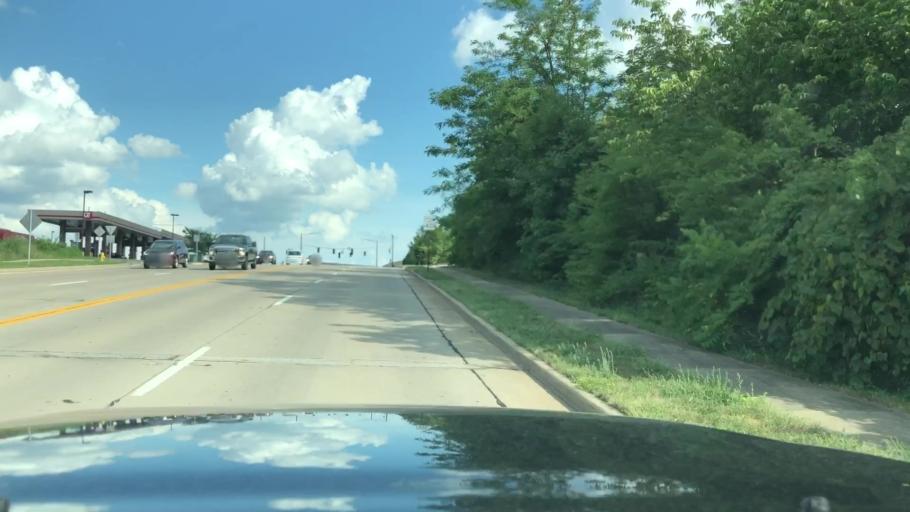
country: US
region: Missouri
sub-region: Saint Charles County
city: Wentzville
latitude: 38.8236
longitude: -90.8547
